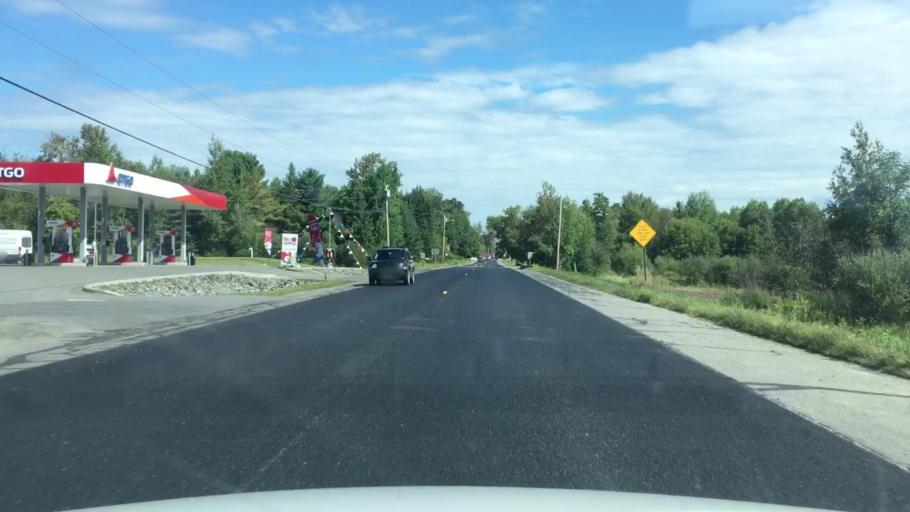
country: US
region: Maine
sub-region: Penobscot County
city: Corinna
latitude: 44.9126
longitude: -69.2644
